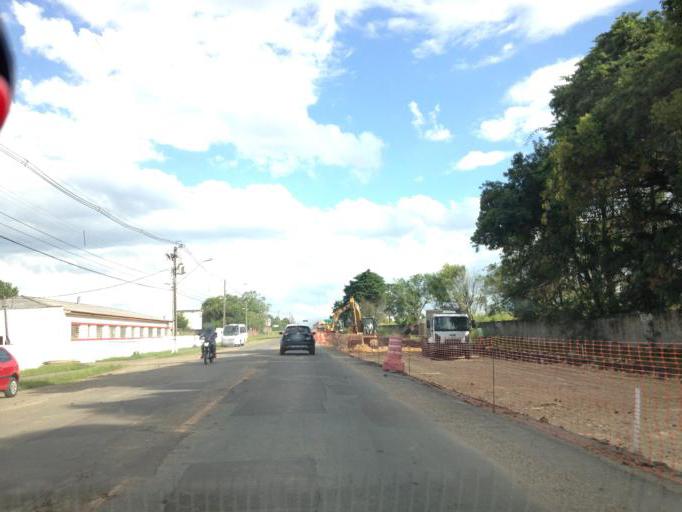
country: BR
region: Parana
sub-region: Pinhais
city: Pinhais
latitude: -25.4188
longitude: -49.2181
